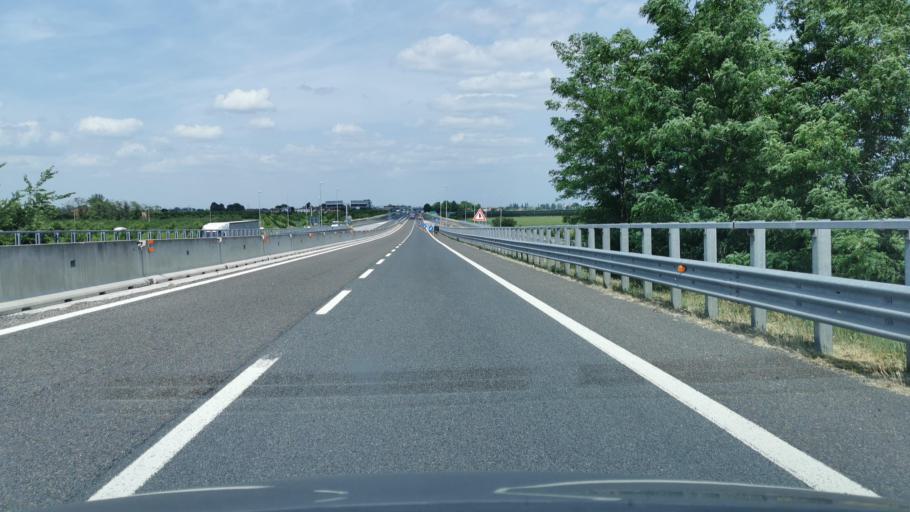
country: IT
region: Emilia-Romagna
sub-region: Provincia di Ravenna
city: Solarolo
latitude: 44.3551
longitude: 11.8171
